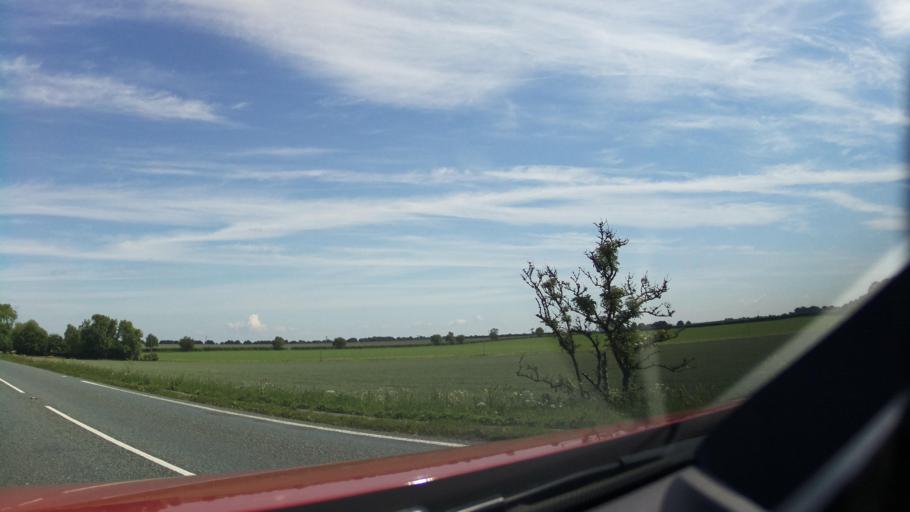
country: GB
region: England
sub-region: Lincolnshire
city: Burton
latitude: 53.2796
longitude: -0.5402
